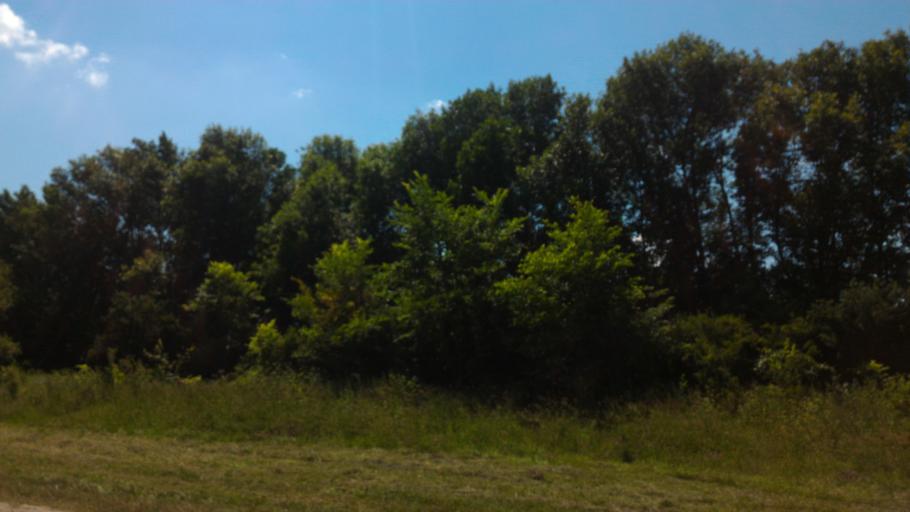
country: RU
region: Rjazan
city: Bagramovo
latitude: 54.7235
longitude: 39.4770
